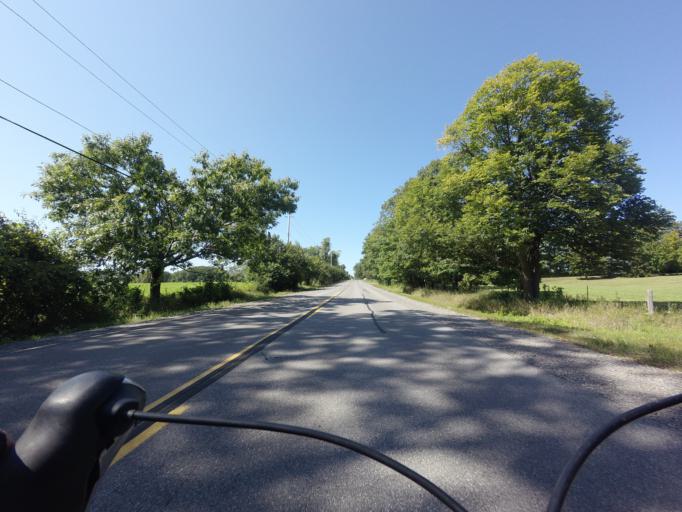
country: CA
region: Ontario
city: Bells Corners
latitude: 45.4101
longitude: -75.9328
